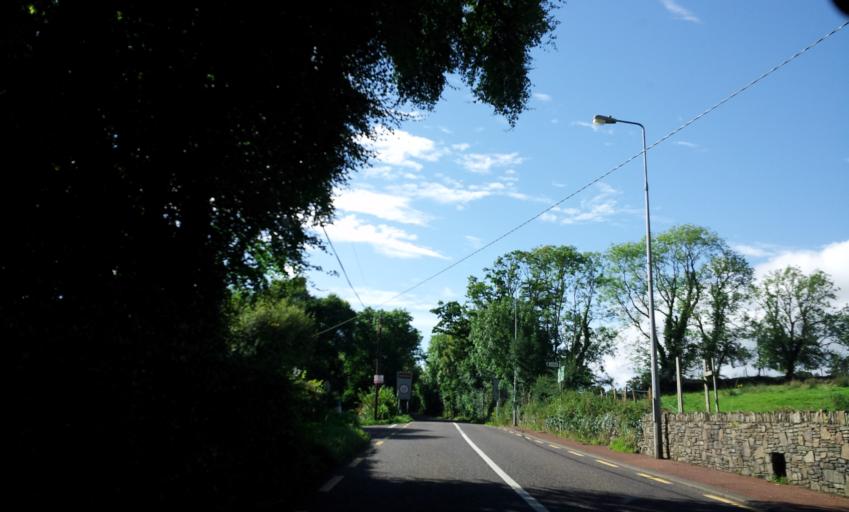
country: IE
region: Munster
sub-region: County Cork
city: Millstreet
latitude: 51.9460
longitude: -9.1742
